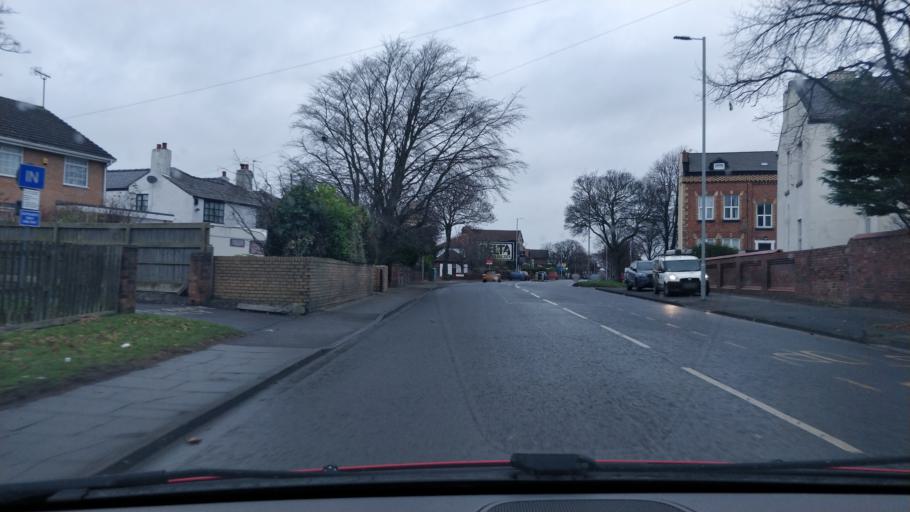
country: GB
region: England
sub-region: Sefton
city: Litherland
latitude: 53.4740
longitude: -2.9975
